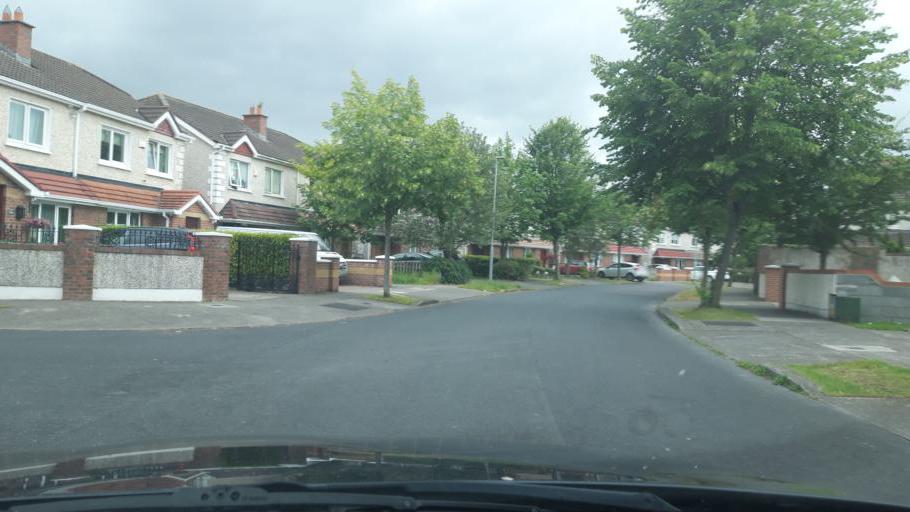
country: IE
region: Leinster
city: Hartstown
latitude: 53.4030
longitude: -6.4168
